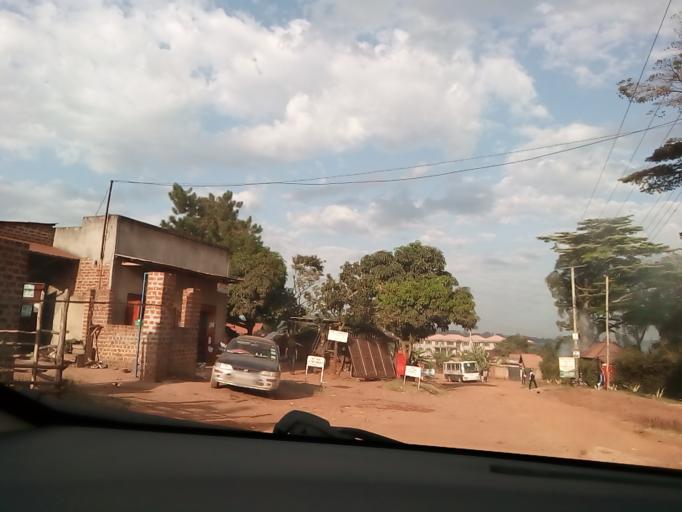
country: UG
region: Central Region
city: Masaka
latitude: -0.3439
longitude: 31.7272
